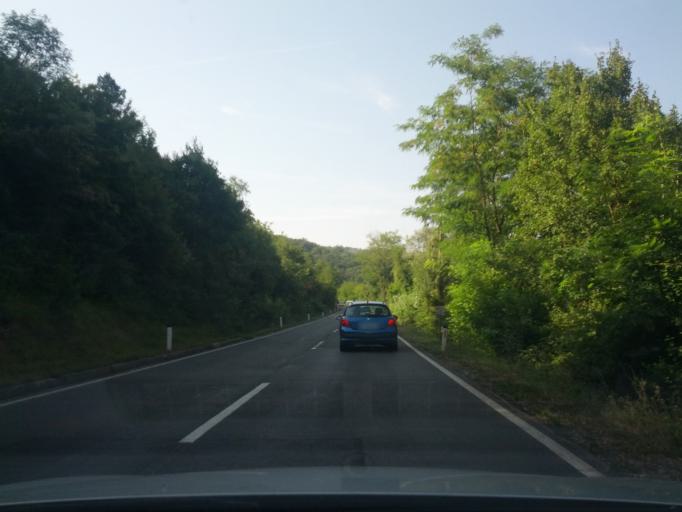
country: SI
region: Izola-Isola
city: Jagodje
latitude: 45.4879
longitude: 13.6776
